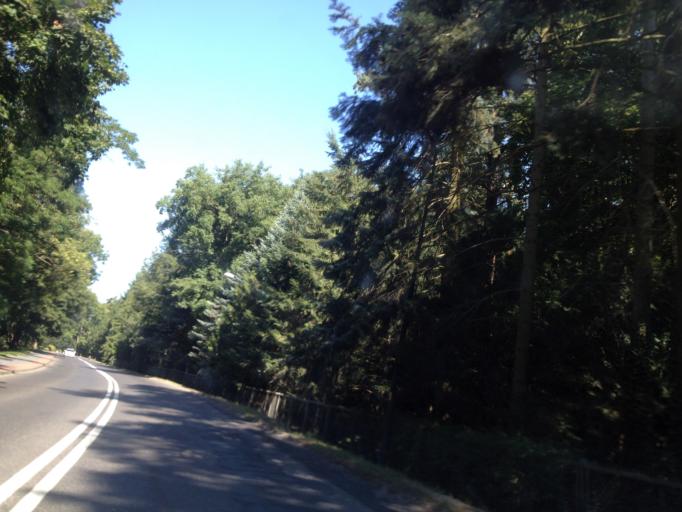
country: PL
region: Greater Poland Voivodeship
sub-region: Powiat poznanski
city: Kornik
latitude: 52.2382
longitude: 17.0926
